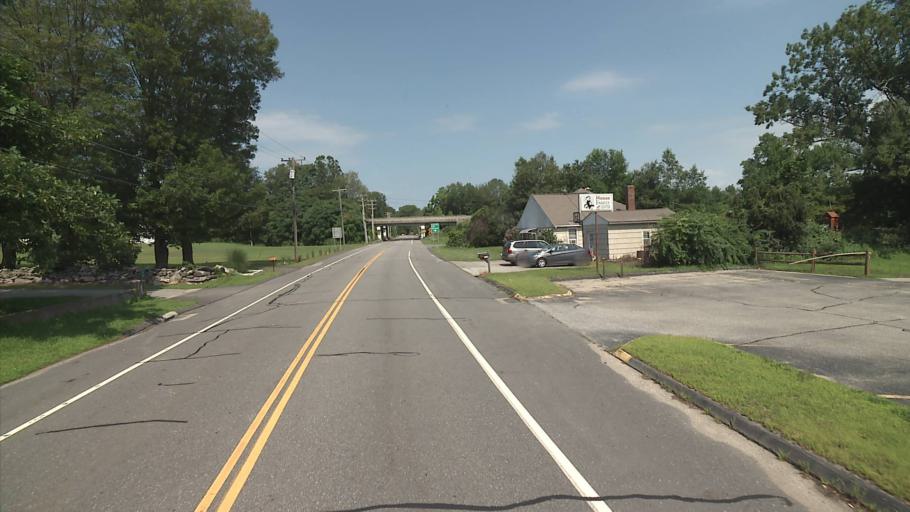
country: US
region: Connecticut
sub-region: New London County
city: Norwich
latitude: 41.5646
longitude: -72.1421
